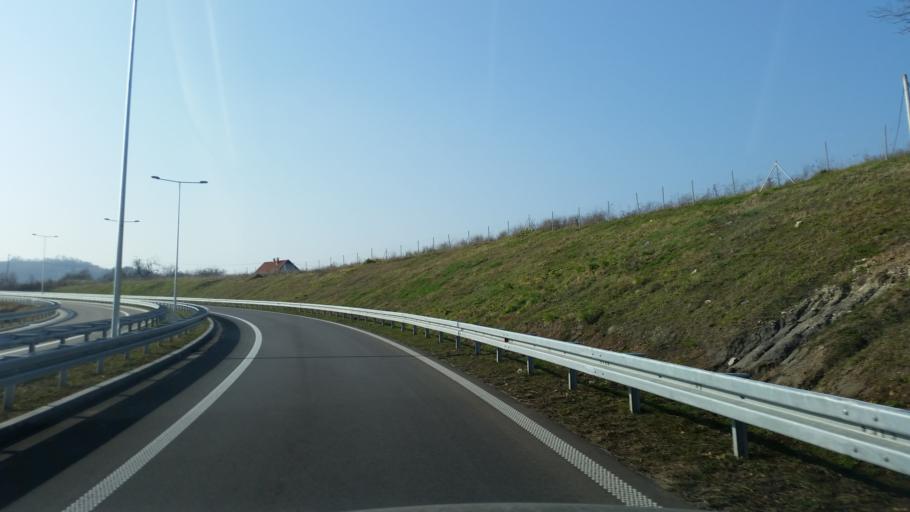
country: RS
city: Prislonica
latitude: 43.9230
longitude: 20.3951
